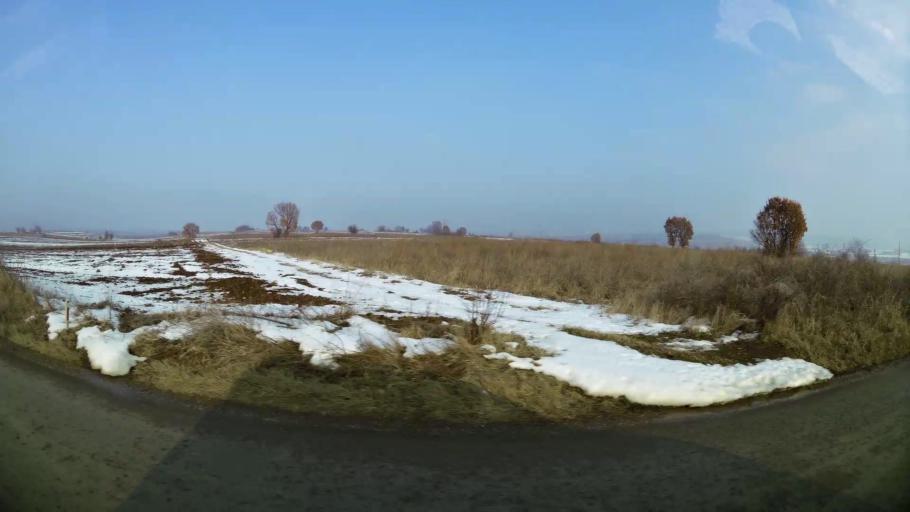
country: MK
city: Miladinovci
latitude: 41.9734
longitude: 21.6328
